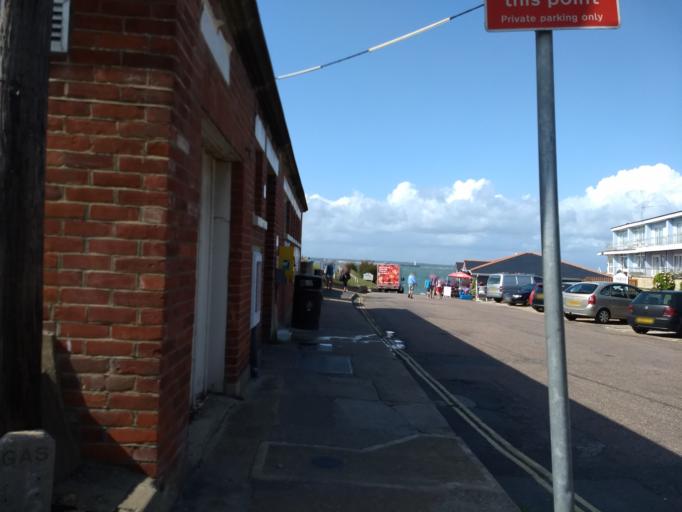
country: GB
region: England
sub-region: Isle of Wight
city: Totland
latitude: 50.6888
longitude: -1.5378
